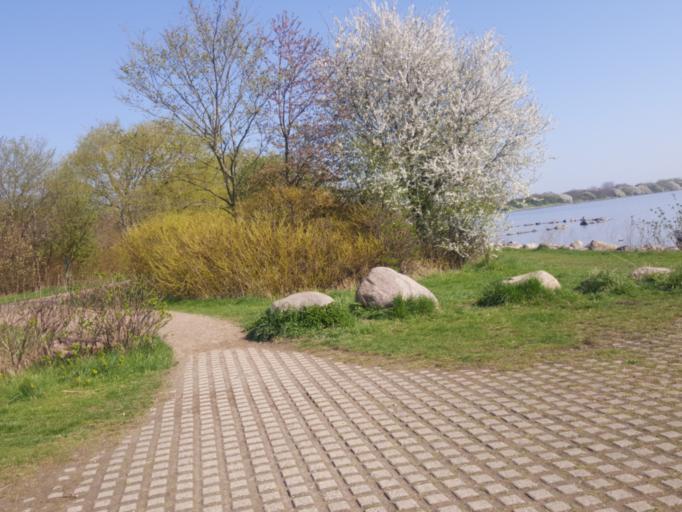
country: DK
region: Capital Region
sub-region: Hvidovre Kommune
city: Hvidovre
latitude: 55.6295
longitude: 12.5035
